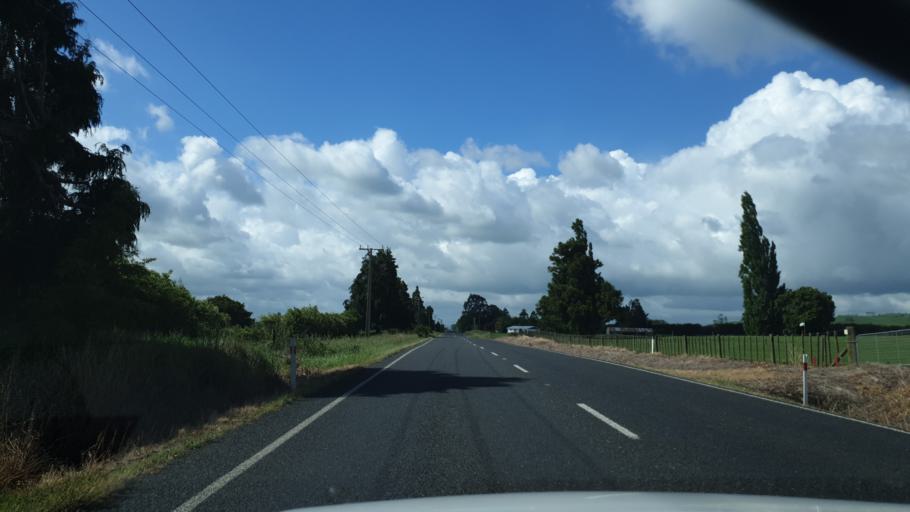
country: NZ
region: Waikato
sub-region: Hauraki District
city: Paeroa
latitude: -37.5069
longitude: 175.4952
